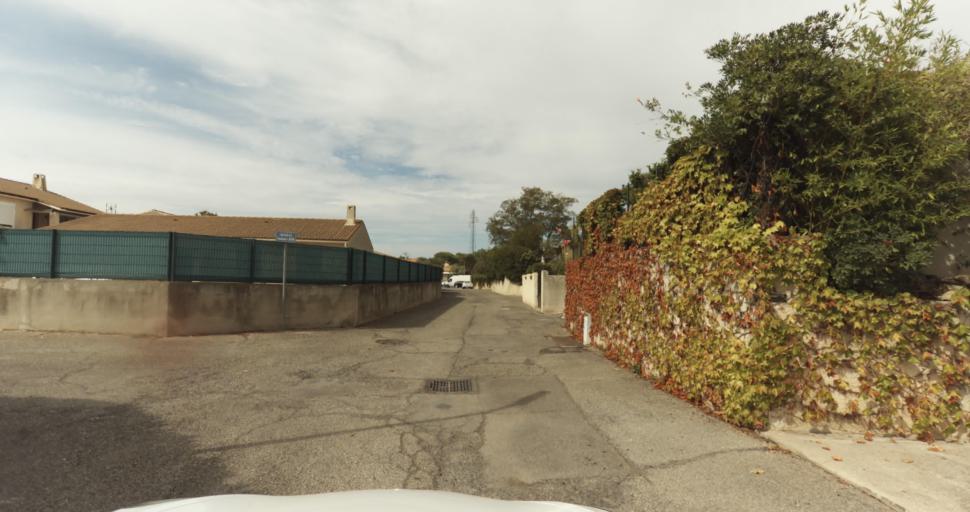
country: FR
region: Provence-Alpes-Cote d'Azur
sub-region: Departement des Bouches-du-Rhone
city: Miramas
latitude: 43.5749
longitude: 5.0110
